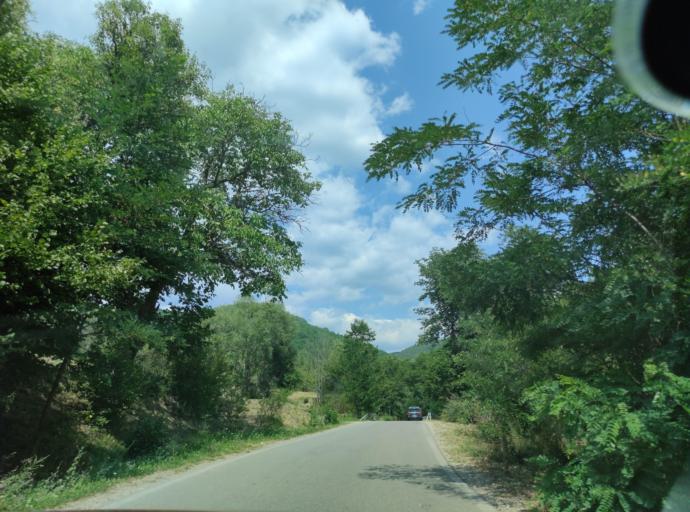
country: BG
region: Blagoevgrad
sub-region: Obshtina Belitsa
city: Belitsa
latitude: 41.9989
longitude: 23.5495
